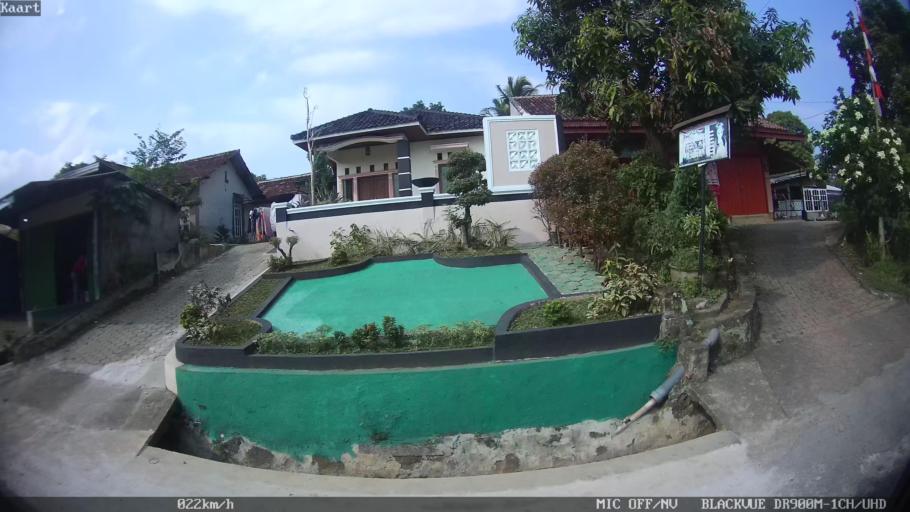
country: ID
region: Lampung
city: Kedaton
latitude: -5.3893
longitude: 105.2070
